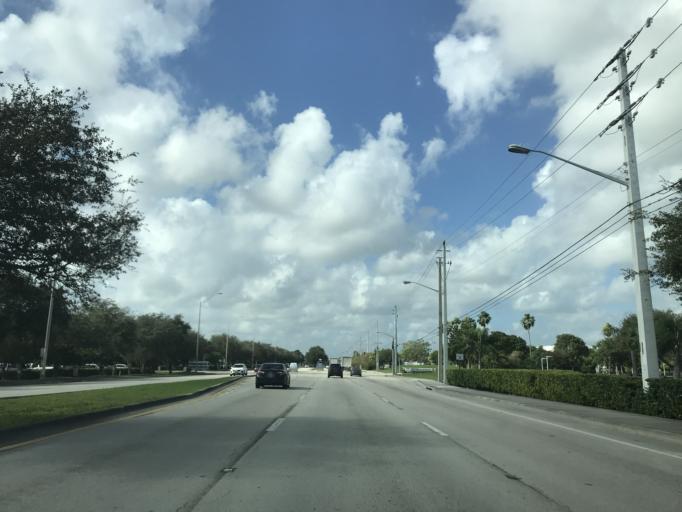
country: US
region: Florida
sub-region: Broward County
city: Coconut Creek
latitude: 26.2601
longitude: -80.1583
